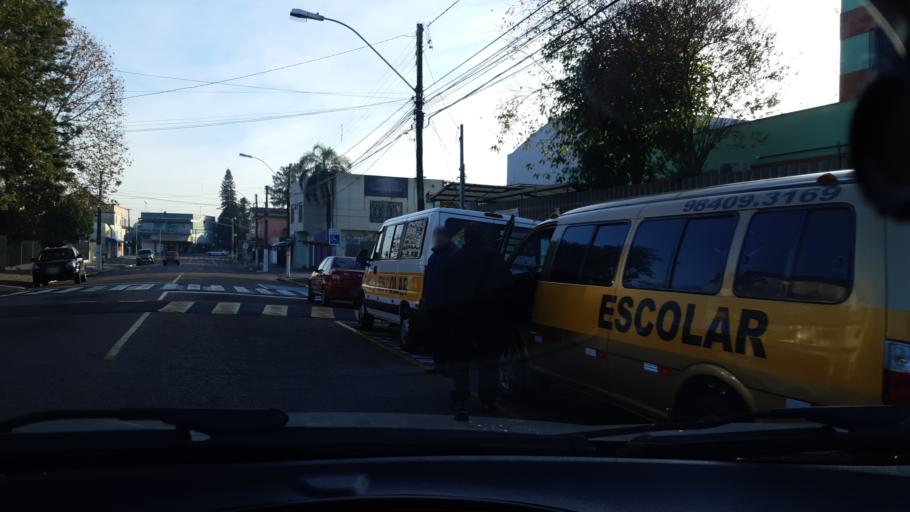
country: BR
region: Rio Grande do Sul
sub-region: Sapucaia Do Sul
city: Sapucaia
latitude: -29.8454
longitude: -51.1526
